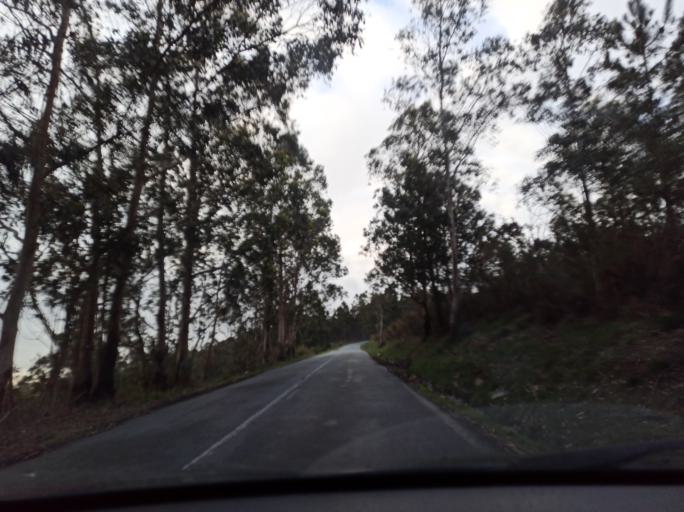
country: ES
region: Galicia
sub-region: Provincia da Coruna
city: Culleredo
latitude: 43.3023
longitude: -8.4295
